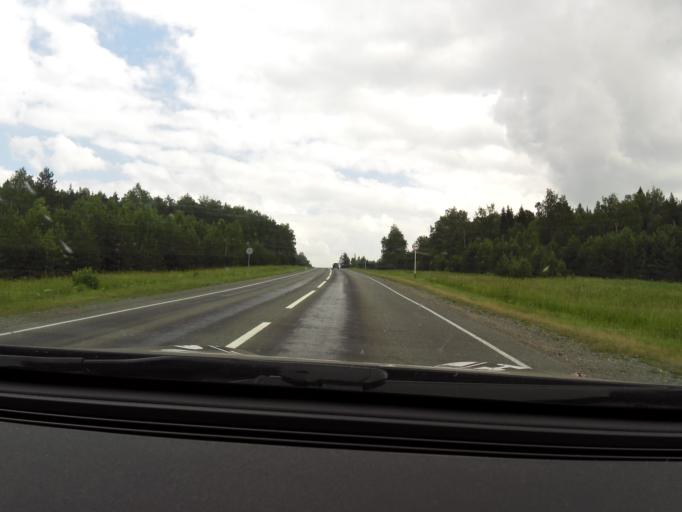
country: RU
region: Perm
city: Suksun
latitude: 56.9256
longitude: 57.5601
